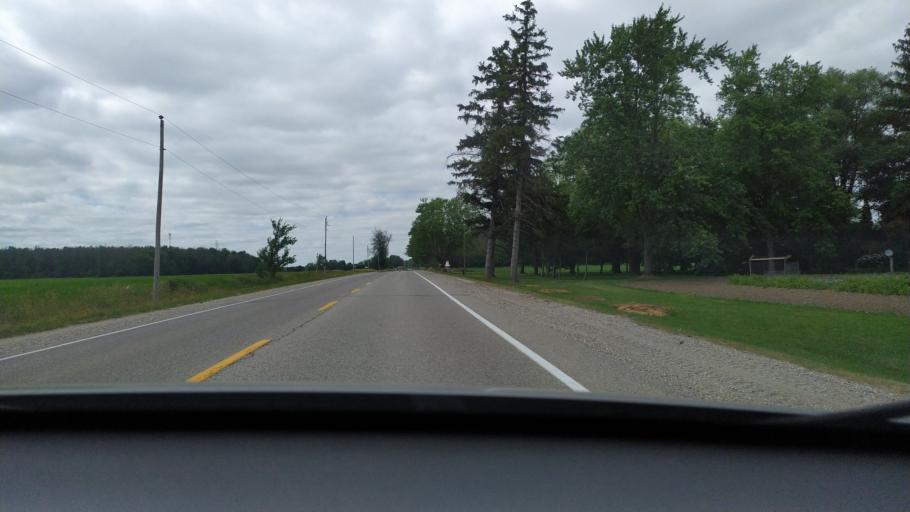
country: CA
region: Ontario
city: Stratford
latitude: 43.3369
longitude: -80.9633
